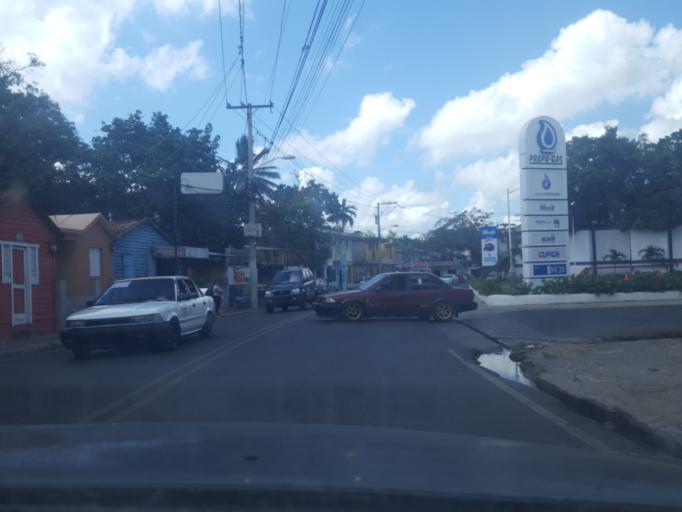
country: DO
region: Santiago
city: Santiago de los Caballeros
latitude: 19.4742
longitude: -70.7103
